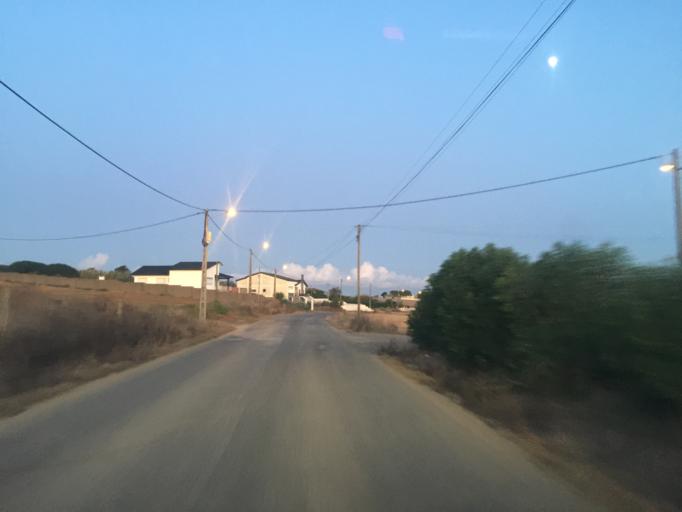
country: PT
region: Leiria
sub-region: Peniche
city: Atouguia da Baleia
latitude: 39.2926
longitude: -9.3097
